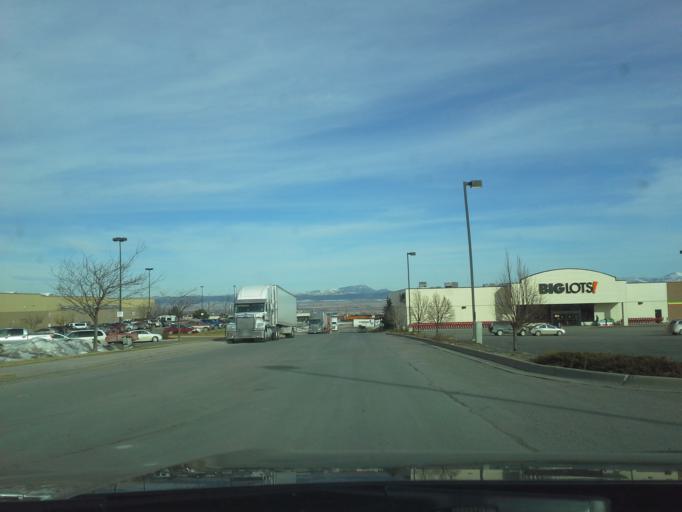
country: US
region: Montana
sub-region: Lewis and Clark County
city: Helena
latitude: 46.5921
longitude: -111.9887
